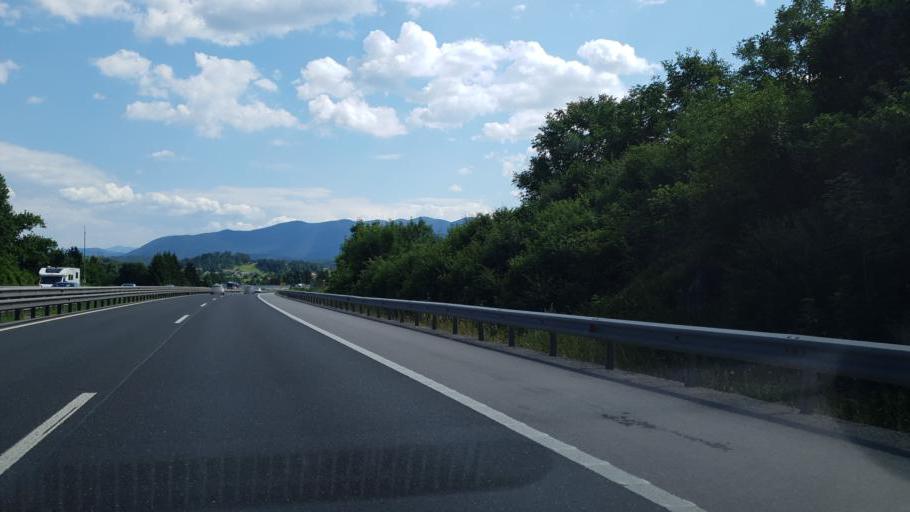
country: SI
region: Cerknica
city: Rakek
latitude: 45.8388
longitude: 14.2937
